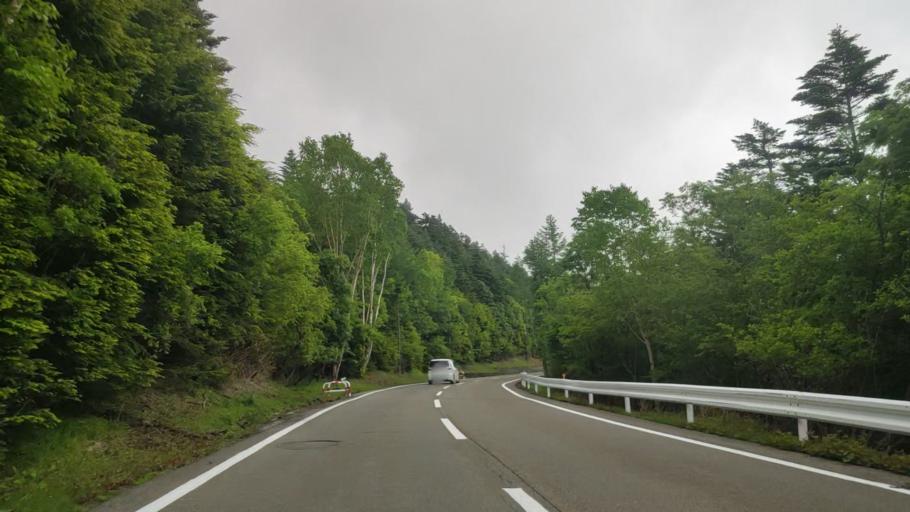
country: JP
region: Yamanashi
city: Fujikawaguchiko
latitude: 35.3837
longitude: 138.6910
